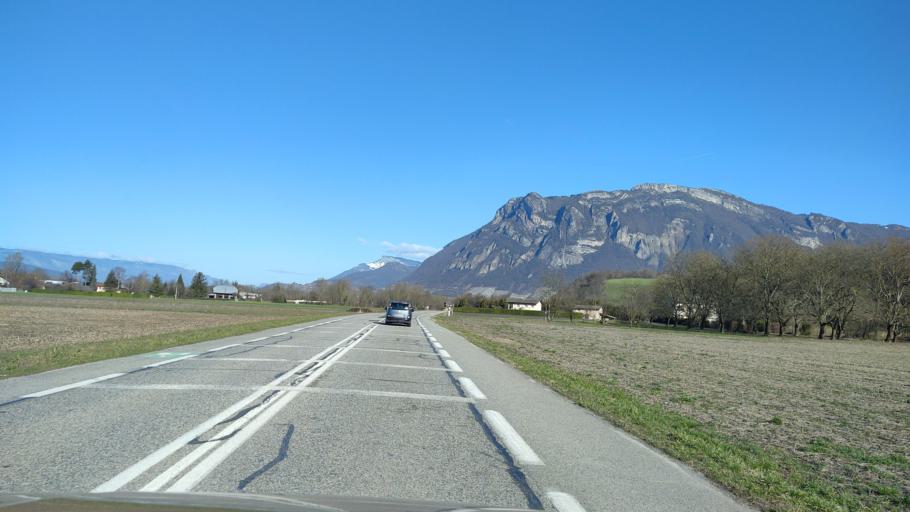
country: FR
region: Rhone-Alpes
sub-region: Departement de la Savoie
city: Montmelian
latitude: 45.4722
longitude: 6.0431
